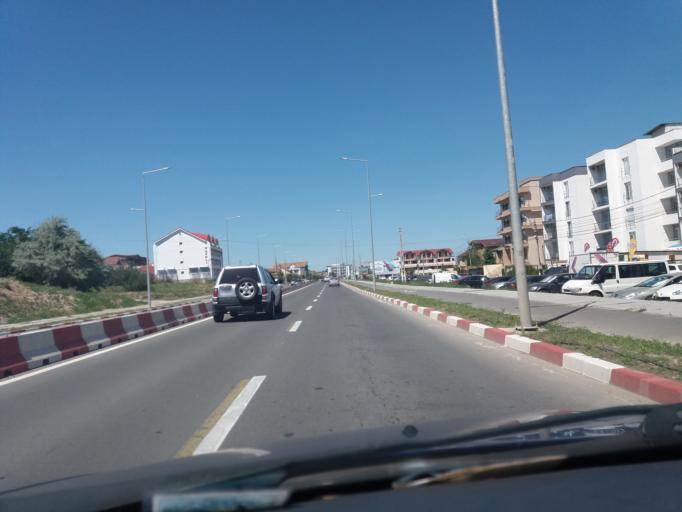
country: RO
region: Constanta
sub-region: Comuna Navodari
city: Navodari
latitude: 44.3041
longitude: 28.6205
